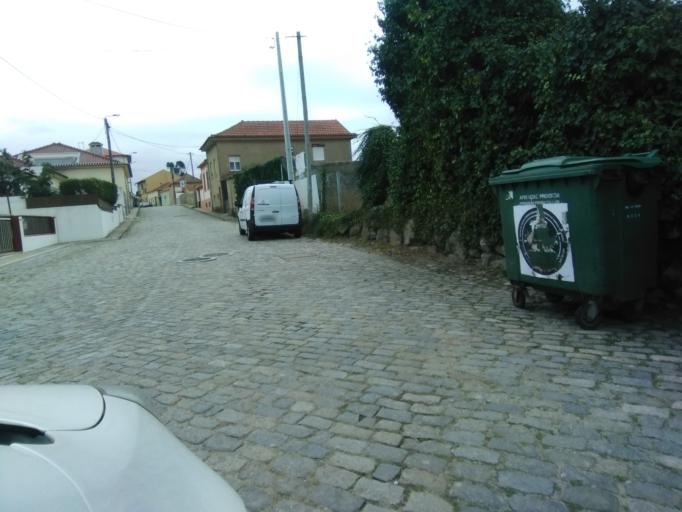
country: PT
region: Porto
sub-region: Matosinhos
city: Lavra
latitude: 41.2317
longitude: -8.7124
